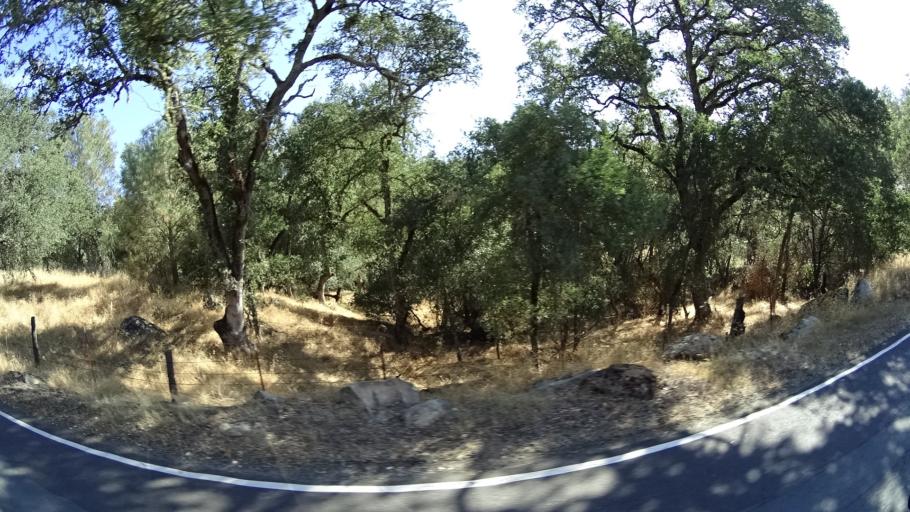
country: US
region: California
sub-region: Calaveras County
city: San Andreas
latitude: 38.1648
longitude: -120.6161
